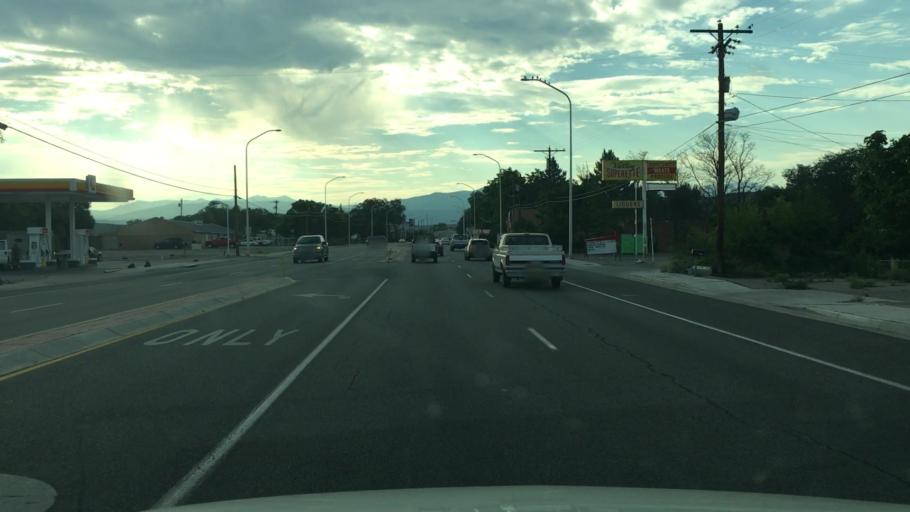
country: US
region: New Mexico
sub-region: Rio Arriba County
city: Espanola
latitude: 35.9881
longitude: -106.0638
